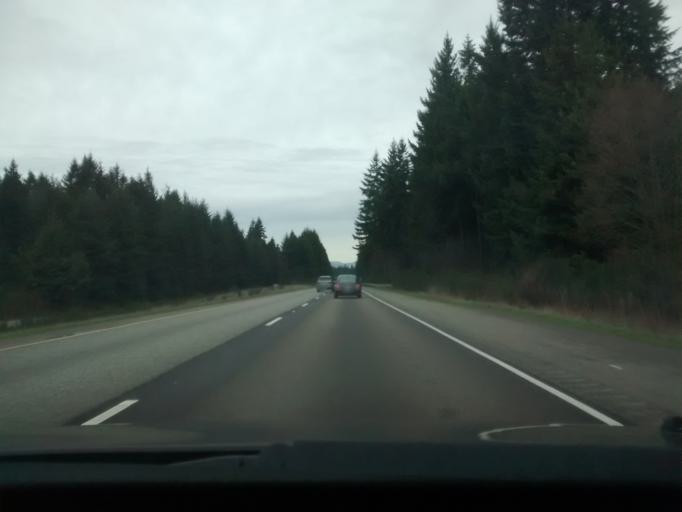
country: US
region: Washington
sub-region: Kitsap County
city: Bethel
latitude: 47.4927
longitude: -122.6372
